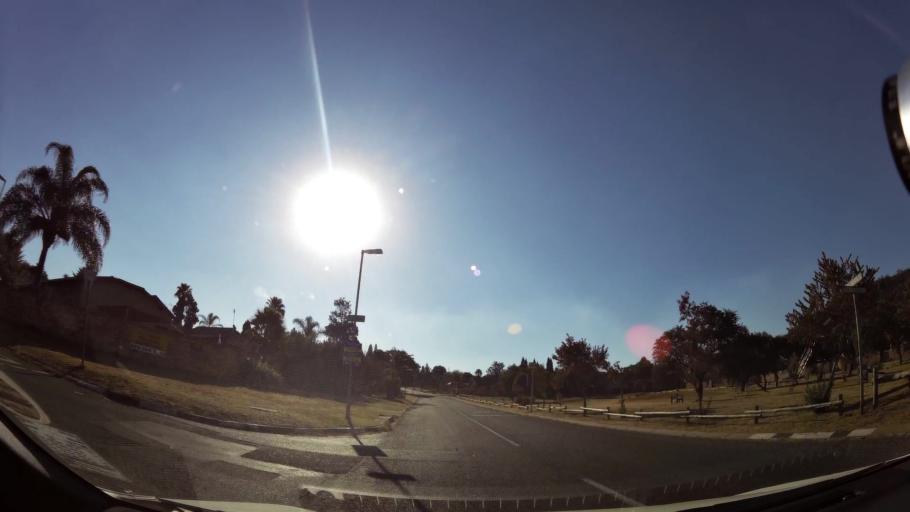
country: ZA
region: Gauteng
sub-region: City of Johannesburg Metropolitan Municipality
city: Johannesburg
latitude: -26.2998
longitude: 28.0618
